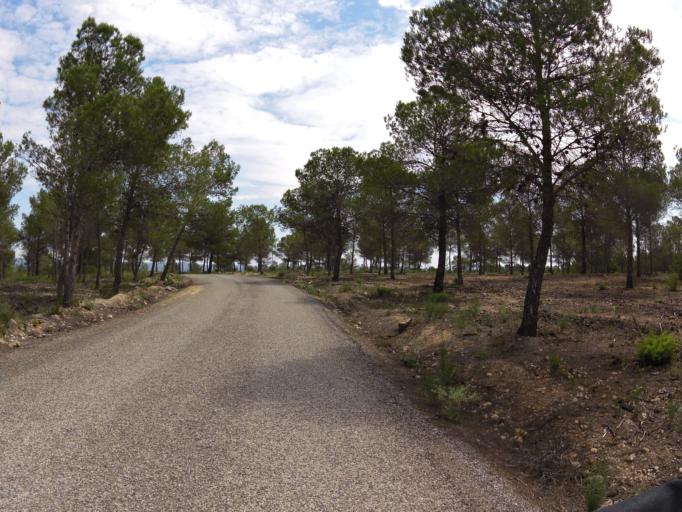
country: ES
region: Castille-La Mancha
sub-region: Provincia de Albacete
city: Casas Ibanez
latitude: 39.3590
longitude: -1.4717
